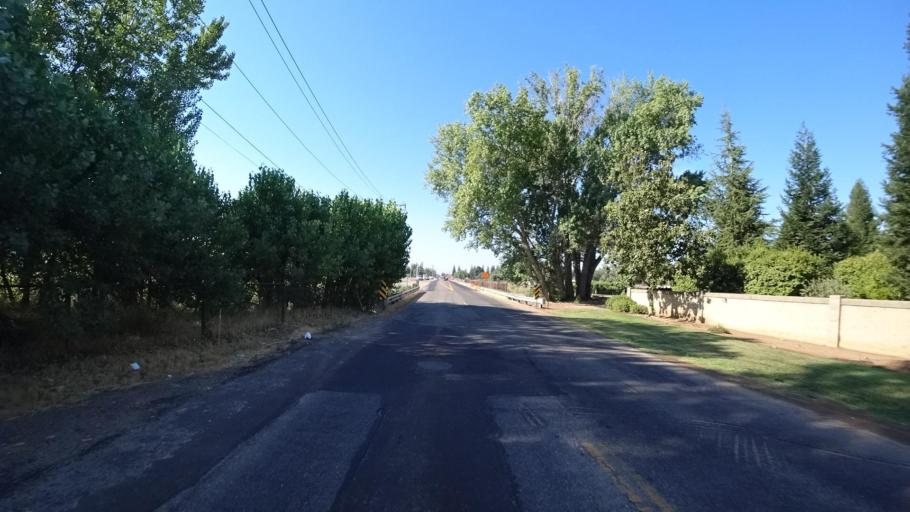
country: US
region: California
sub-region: Fresno County
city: Sunnyside
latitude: 36.7674
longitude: -119.6641
